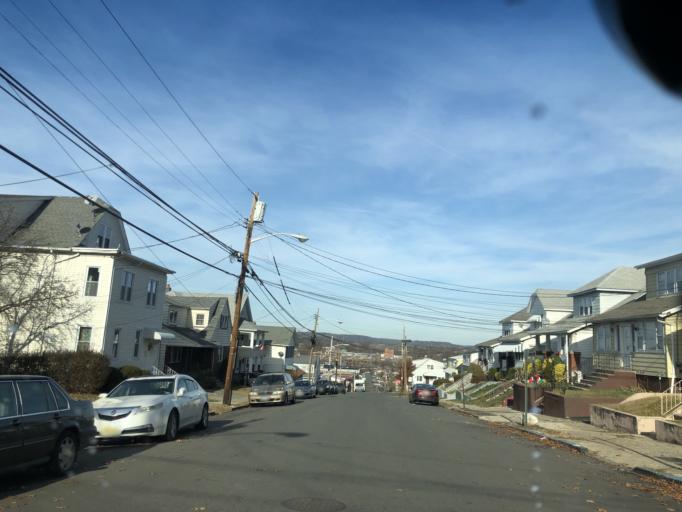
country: US
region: New Jersey
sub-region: Bergen County
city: Fair Lawn
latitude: 40.9341
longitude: -74.1460
